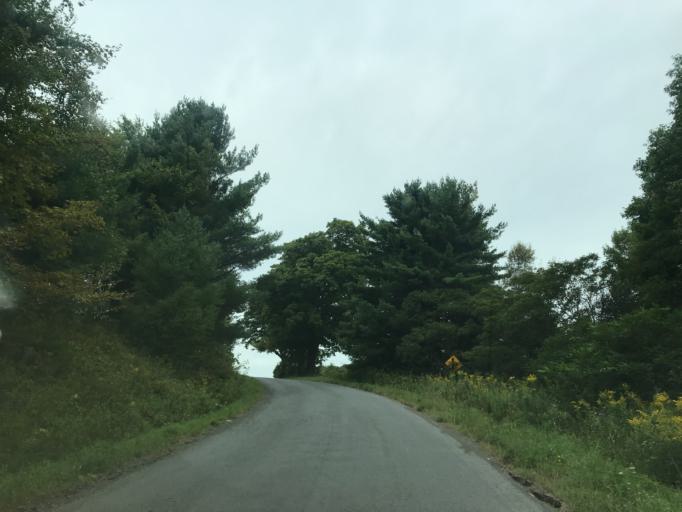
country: US
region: New York
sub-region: Otsego County
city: Worcester
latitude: 42.5803
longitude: -74.6720
